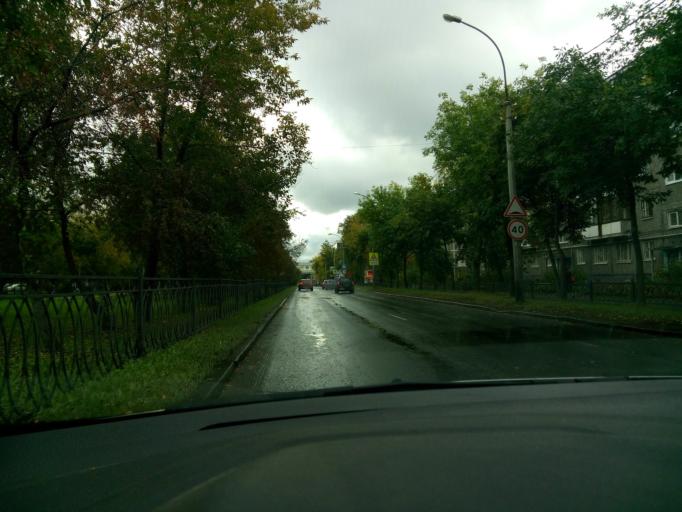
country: RU
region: Sverdlovsk
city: Yekaterinburg
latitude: 56.8188
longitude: 60.5811
